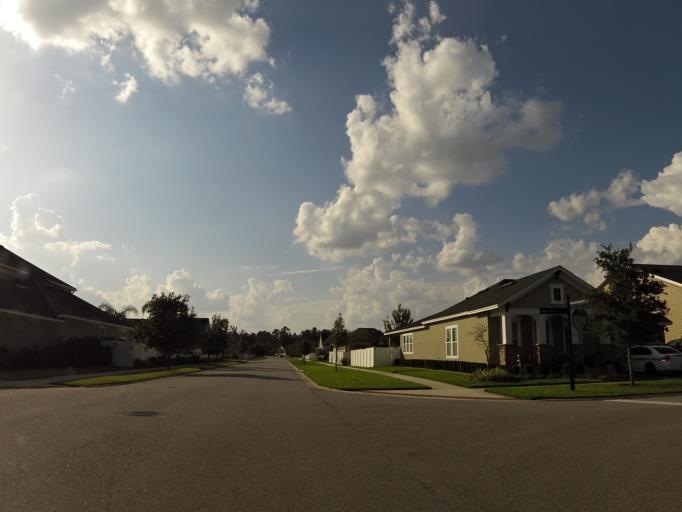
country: US
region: Florida
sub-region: Clay County
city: Green Cove Springs
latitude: 30.0246
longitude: -81.6360
